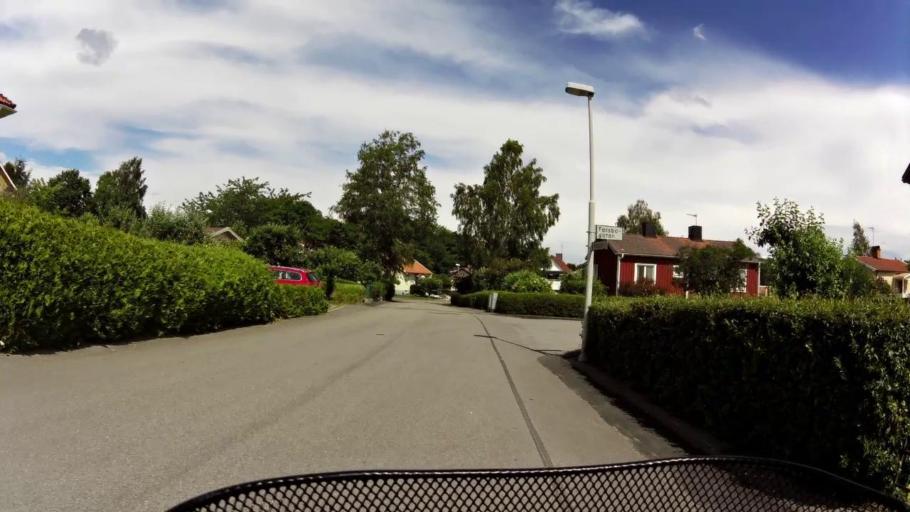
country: SE
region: OEstergoetland
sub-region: Linkopings Kommun
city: Malmslatt
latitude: 58.4150
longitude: 15.5213
